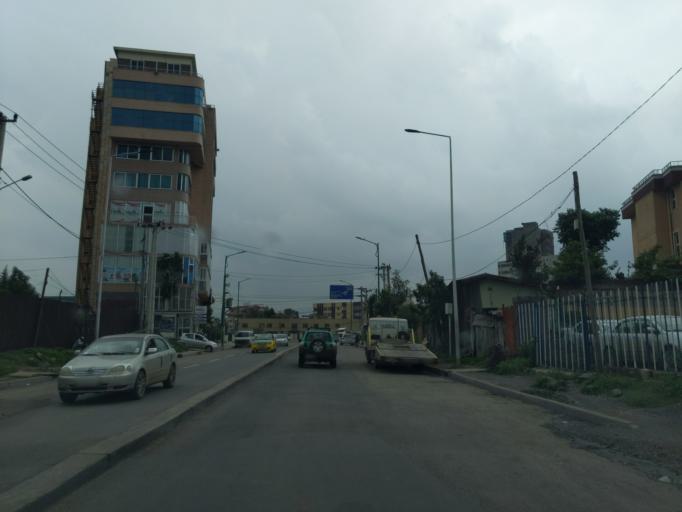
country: ET
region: Adis Abeba
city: Addis Ababa
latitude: 8.9864
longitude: 38.7652
